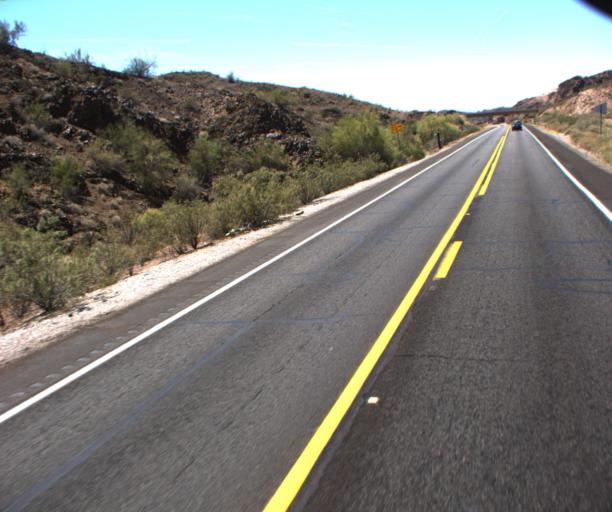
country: US
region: Arizona
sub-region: La Paz County
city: Cienega Springs
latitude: 34.2562
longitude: -114.1560
